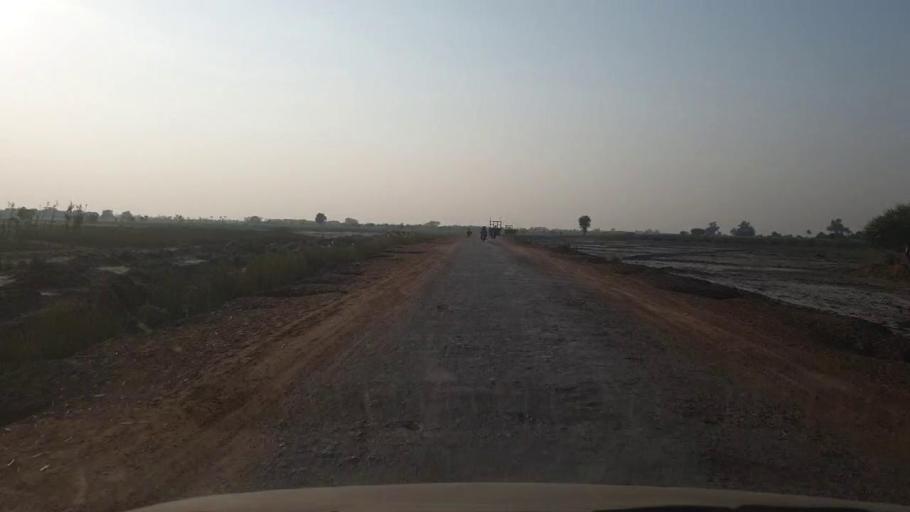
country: PK
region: Sindh
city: Mirwah Gorchani
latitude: 25.3683
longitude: 69.1346
